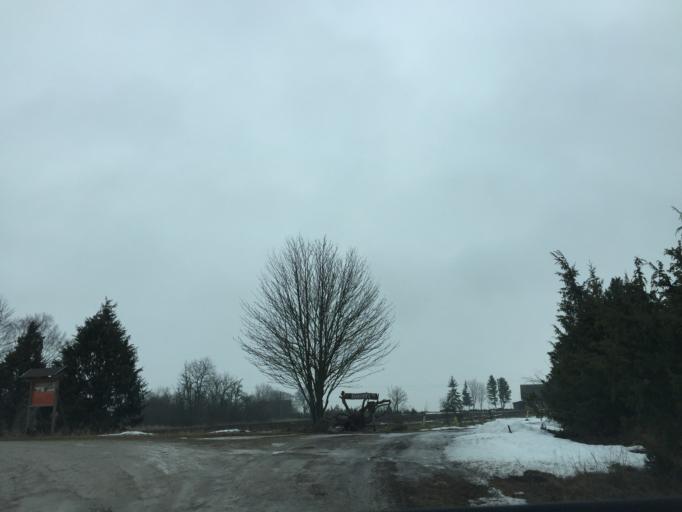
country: EE
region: Saare
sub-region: Orissaare vald
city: Orissaare
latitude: 58.5768
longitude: 23.3723
